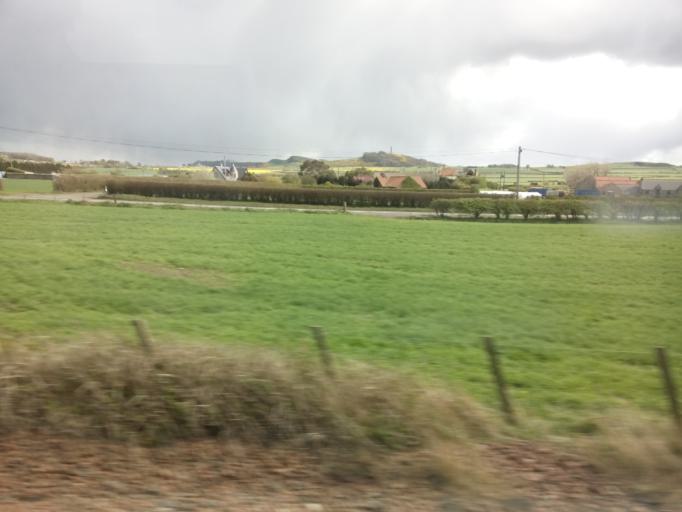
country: GB
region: Scotland
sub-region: East Lothian
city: Gullane
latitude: 55.9948
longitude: -2.8288
